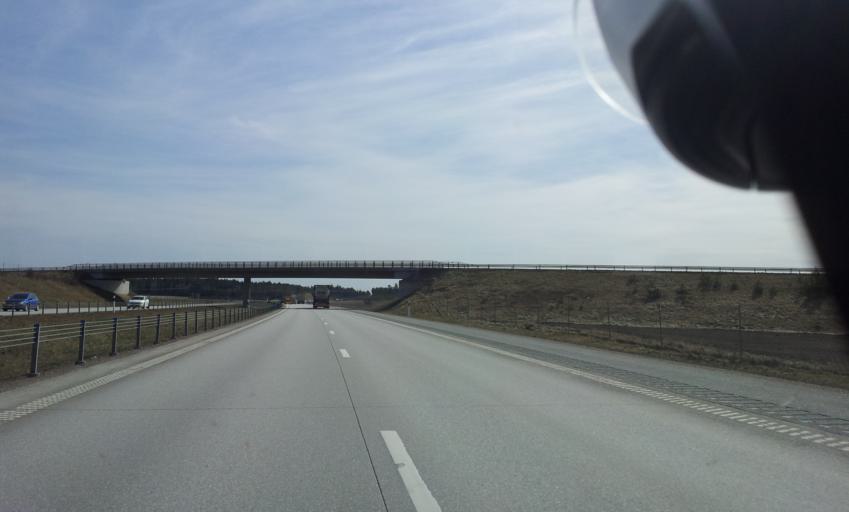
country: SE
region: Uppsala
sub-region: Uppsala Kommun
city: Storvreta
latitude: 59.9814
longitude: 17.6398
